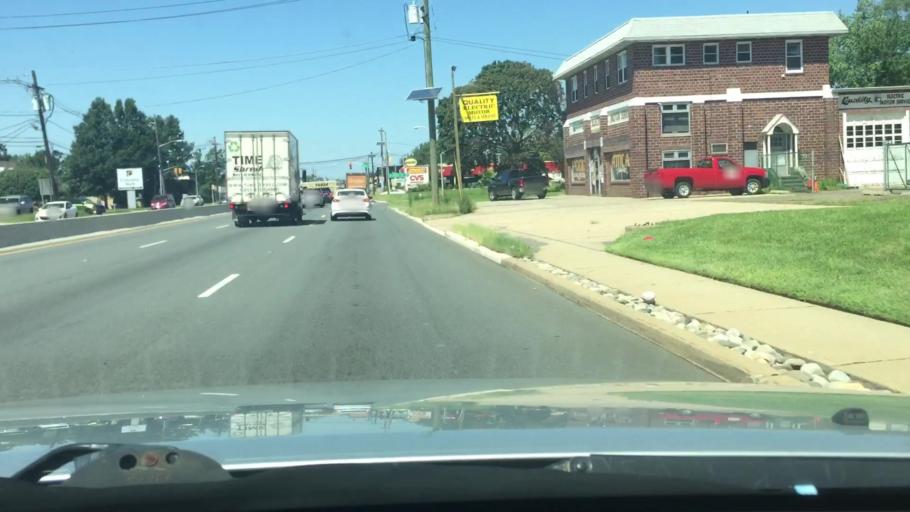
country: US
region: New Jersey
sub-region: Middlesex County
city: South River
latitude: 40.4487
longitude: -74.3968
